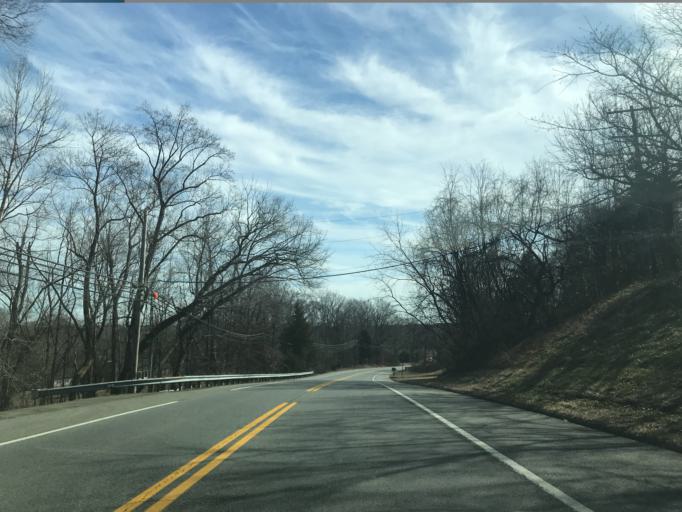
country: US
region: Maryland
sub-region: Charles County
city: Potomac Heights
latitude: 38.5970
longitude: -77.1253
